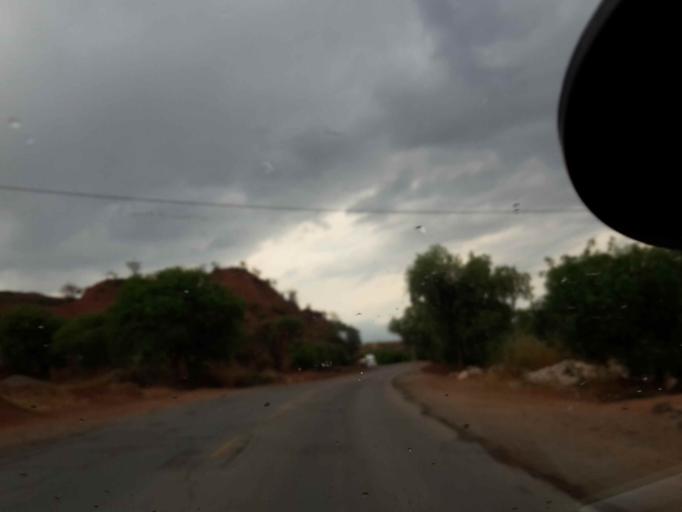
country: BO
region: Cochabamba
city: Sipe Sipe
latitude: -17.4868
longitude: -66.3383
